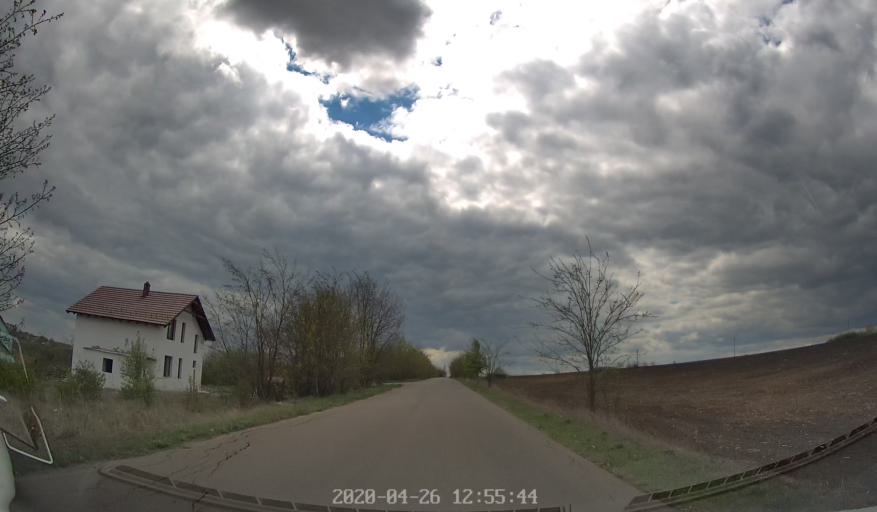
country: MD
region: Chisinau
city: Vadul lui Voda
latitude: 47.0771
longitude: 29.0665
